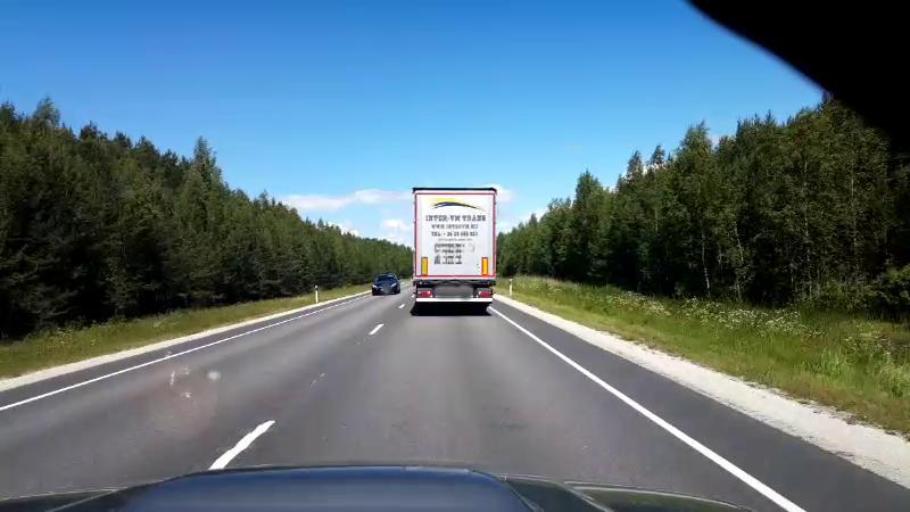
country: EE
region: Paernumaa
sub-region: Paernu linn
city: Parnu
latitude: 58.1238
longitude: 24.5117
